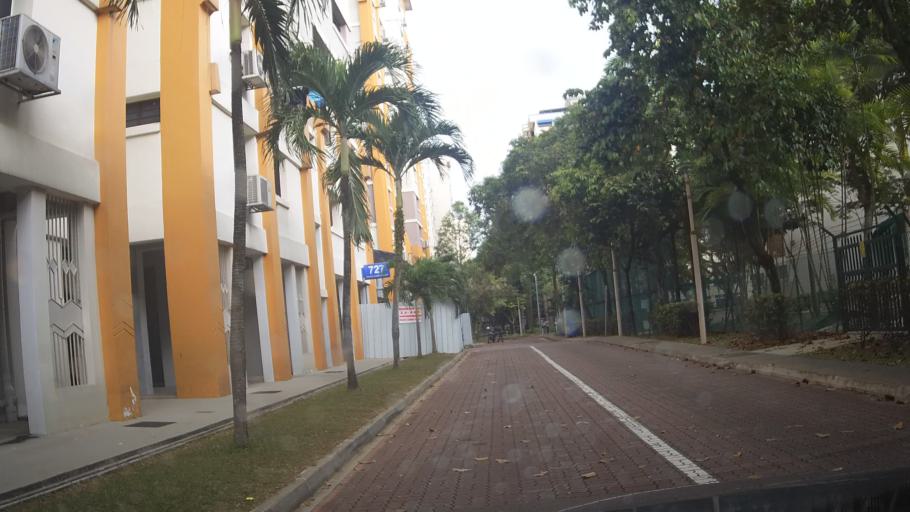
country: MY
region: Johor
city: Johor Bahru
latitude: 1.4437
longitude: 103.7999
